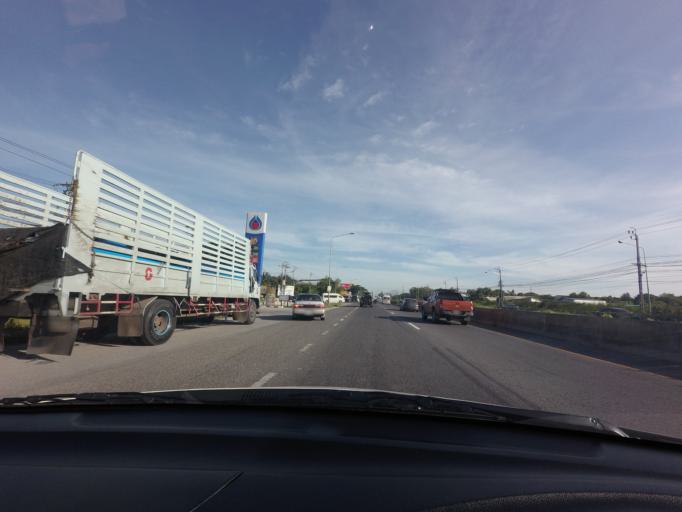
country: TH
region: Nonthaburi
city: Bang Bua Thong
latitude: 13.9577
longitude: 100.4050
